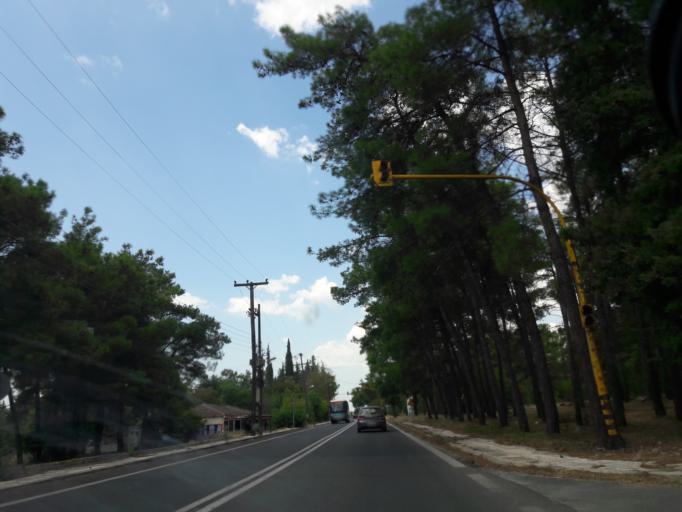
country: GR
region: Central Macedonia
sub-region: Nomos Thessalonikis
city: Souroti
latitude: 40.5124
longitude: 23.0775
